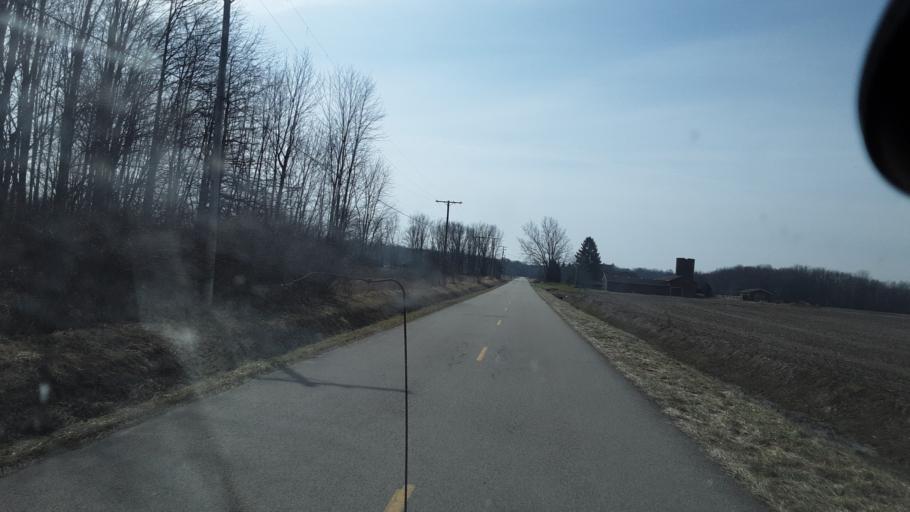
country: US
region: Ohio
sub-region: Ashtabula County
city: Jefferson
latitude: 41.7552
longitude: -80.7415
